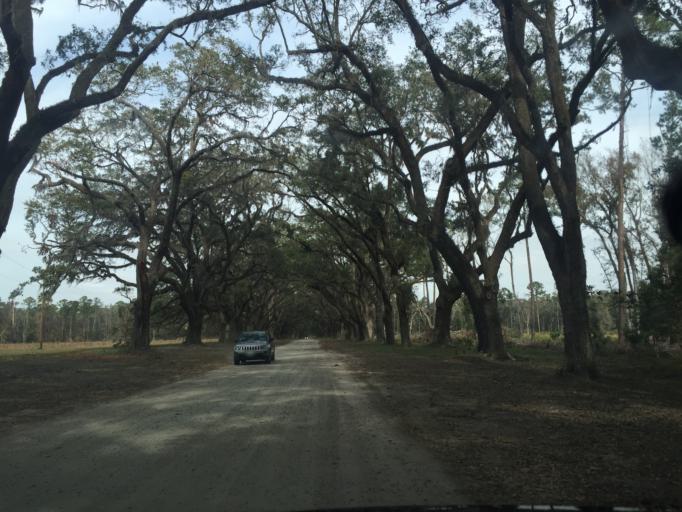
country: US
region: Georgia
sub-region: Chatham County
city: Isle of Hope
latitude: 31.9677
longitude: -81.0692
